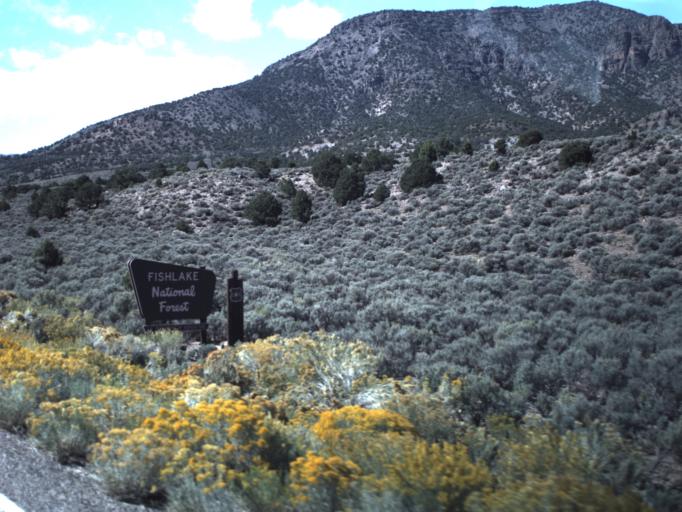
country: US
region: Utah
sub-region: Piute County
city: Junction
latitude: 38.2617
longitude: -112.2528
